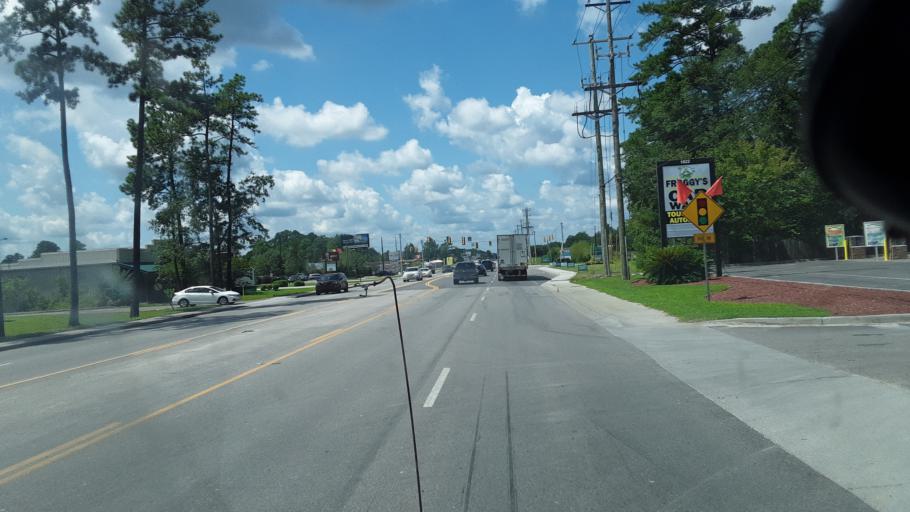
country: US
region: South Carolina
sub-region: Berkeley County
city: Sangaree
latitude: 33.0427
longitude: -80.1272
